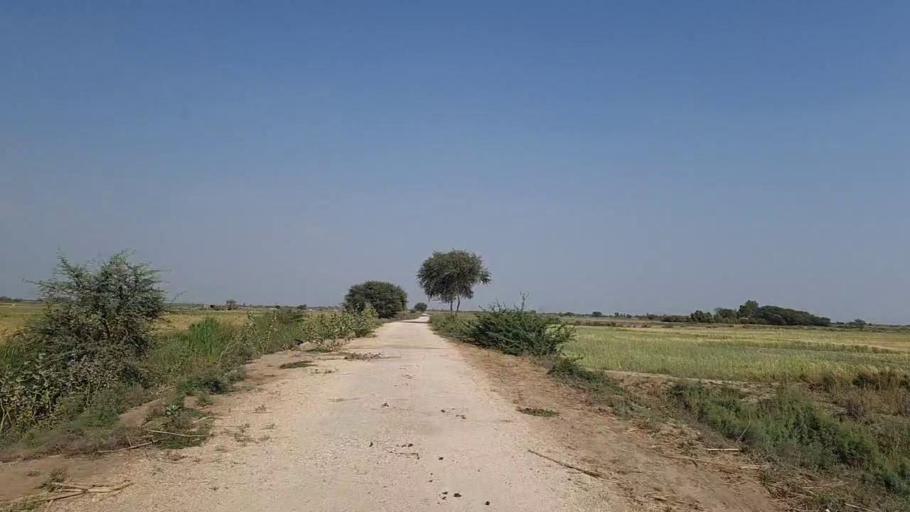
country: PK
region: Sindh
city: Daro Mehar
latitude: 24.7590
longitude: 68.1598
